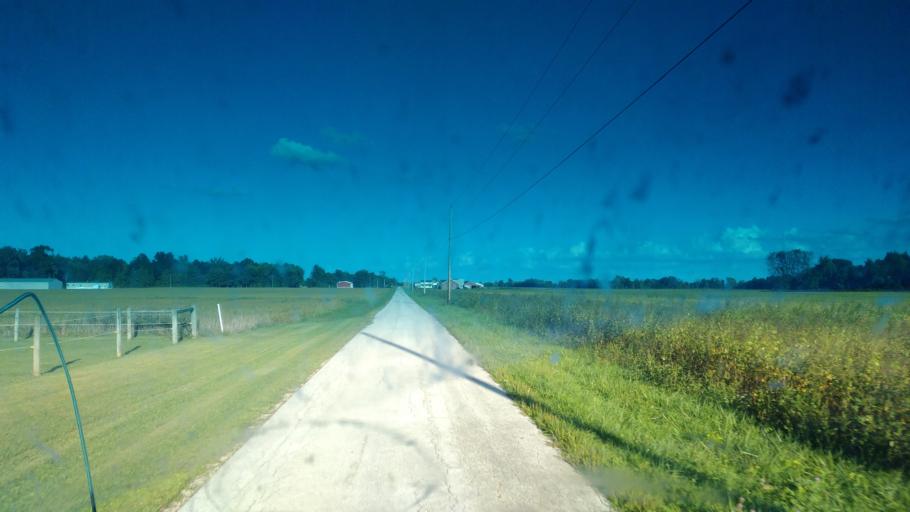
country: US
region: Ohio
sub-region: Wyandot County
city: Carey
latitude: 40.9413
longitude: -83.4541
